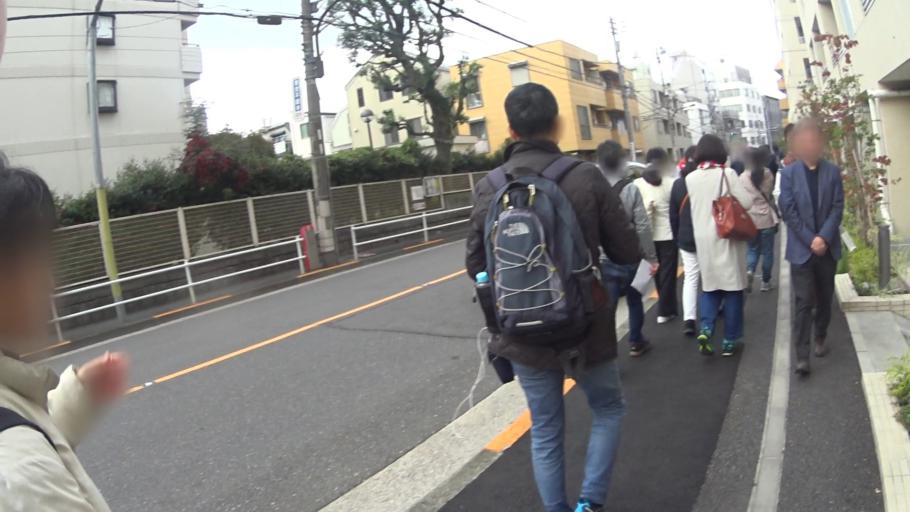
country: JP
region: Tokyo
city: Tokyo
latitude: 35.7016
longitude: 139.7328
